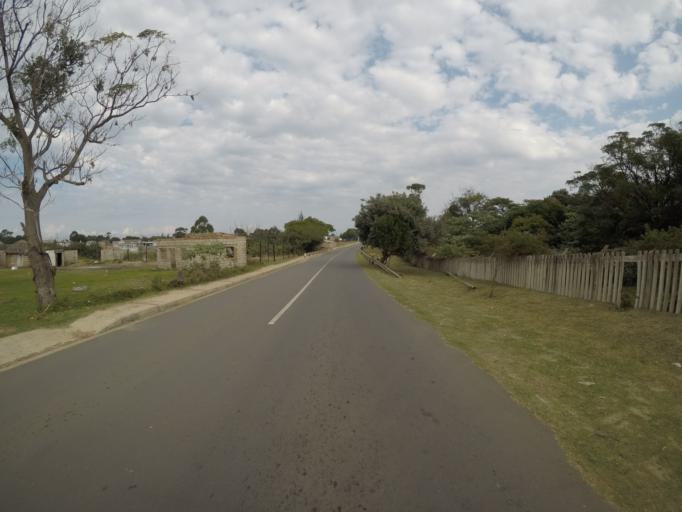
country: ZA
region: KwaZulu-Natal
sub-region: uThungulu District Municipality
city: Richards Bay
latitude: -28.7396
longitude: 32.0949
